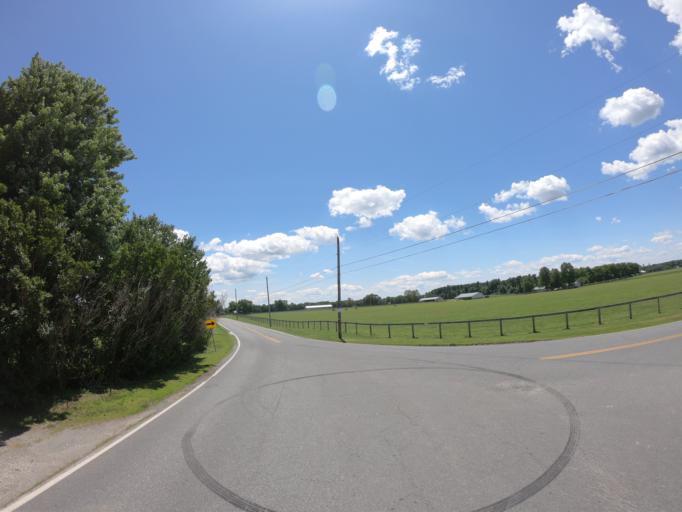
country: US
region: Delaware
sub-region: New Castle County
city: Middletown
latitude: 39.4763
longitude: -75.7793
